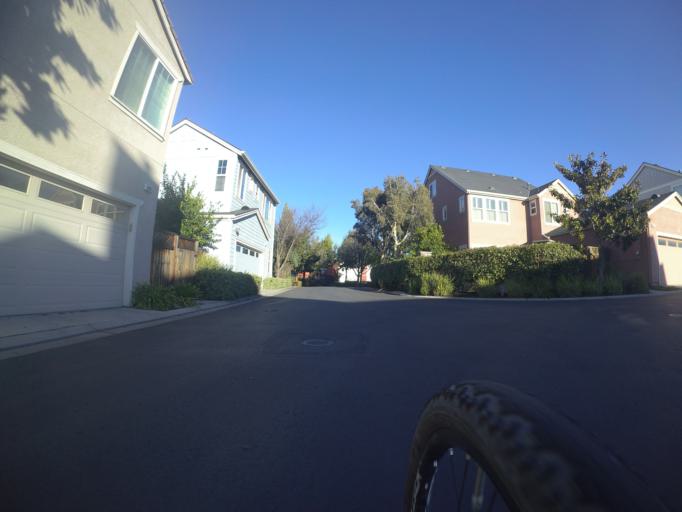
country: US
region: California
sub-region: Santa Clara County
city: Santa Clara
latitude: 37.3986
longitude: -121.9492
